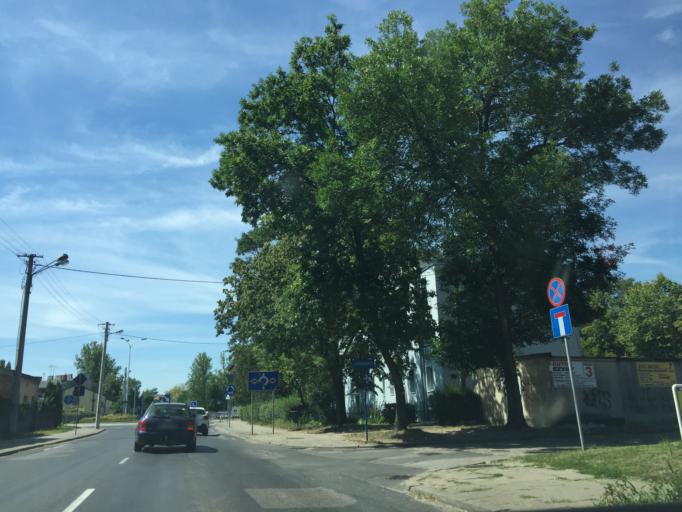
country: PL
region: Lodz Voivodeship
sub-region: Piotrkow Trybunalski
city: Piotrkow Trybunalski
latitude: 51.4116
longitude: 19.7064
